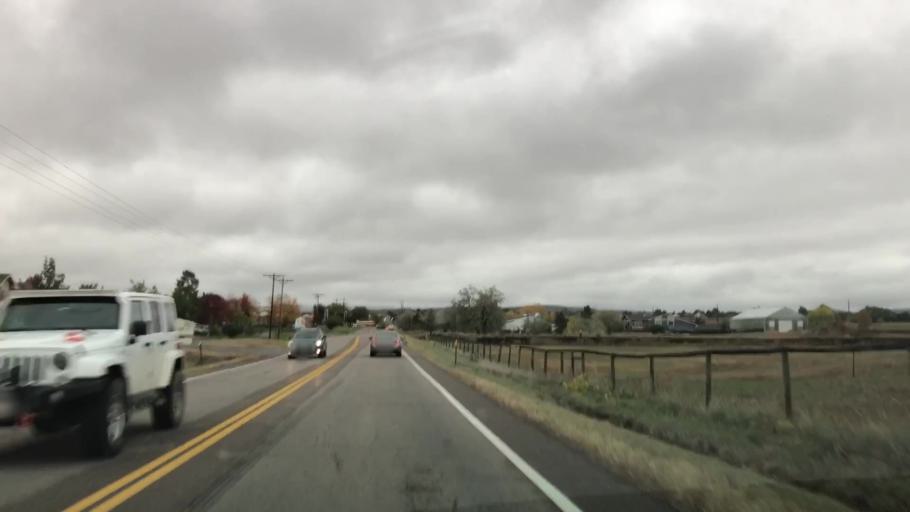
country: US
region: Colorado
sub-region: Larimer County
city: Loveland
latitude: 40.4802
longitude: -105.0718
